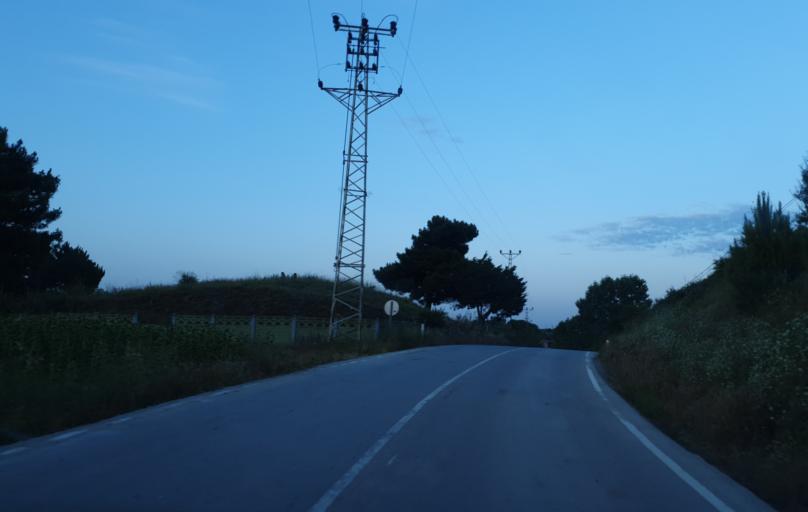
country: TR
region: Tekirdag
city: Velimese
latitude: 41.3502
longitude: 27.8757
